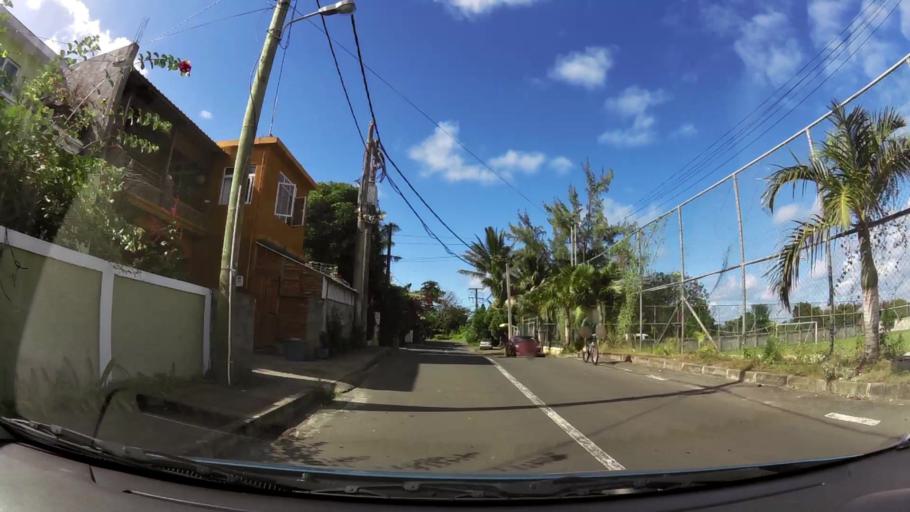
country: MU
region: Grand Port
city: Beau Vallon
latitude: -20.4222
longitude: 57.7171
